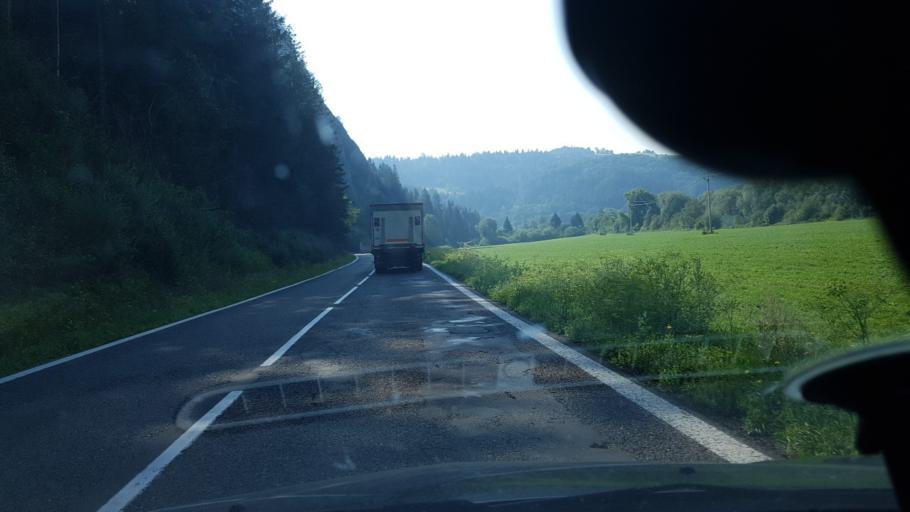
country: SK
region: Zilinsky
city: Tvrdosin
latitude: 49.2979
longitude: 19.4864
